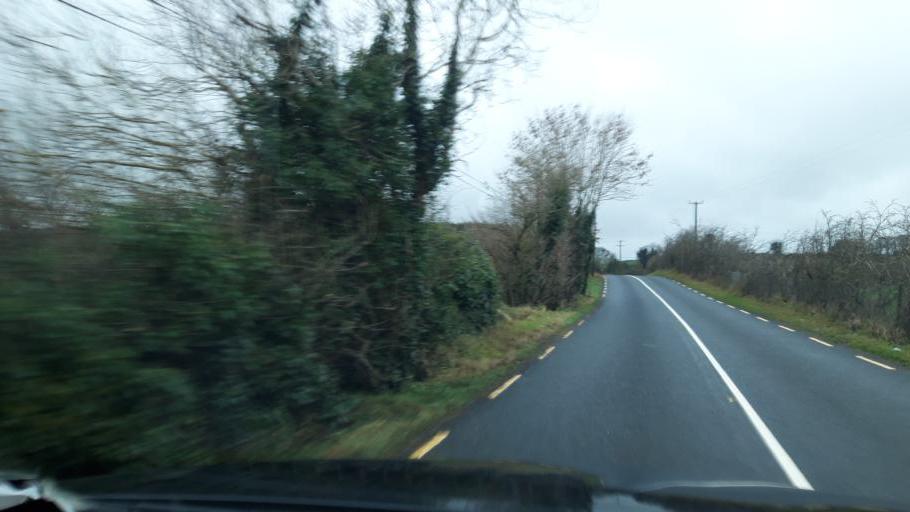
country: IE
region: Ulster
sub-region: County Monaghan
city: Castleblayney
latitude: 54.0765
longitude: -6.6823
